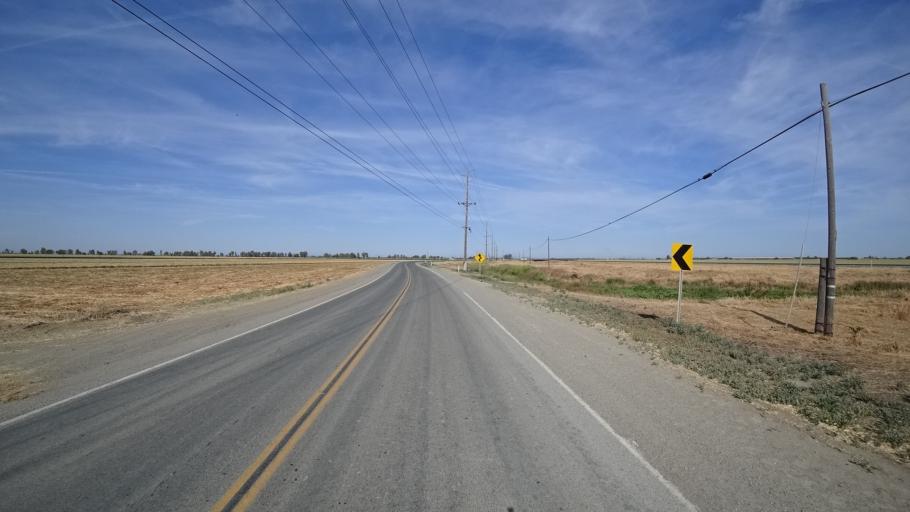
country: US
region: California
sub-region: Tulare County
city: Goshen
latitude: 36.3430
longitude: -119.5233
